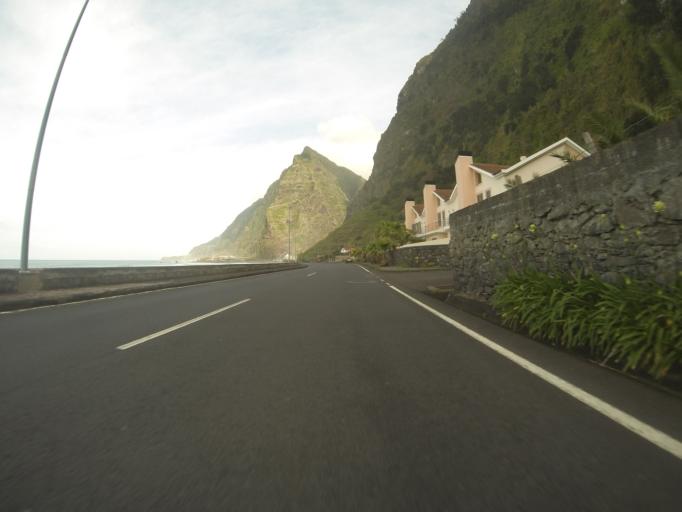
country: PT
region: Madeira
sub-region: Sao Vicente
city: Sao Vicente
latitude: 32.8093
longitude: -17.0593
